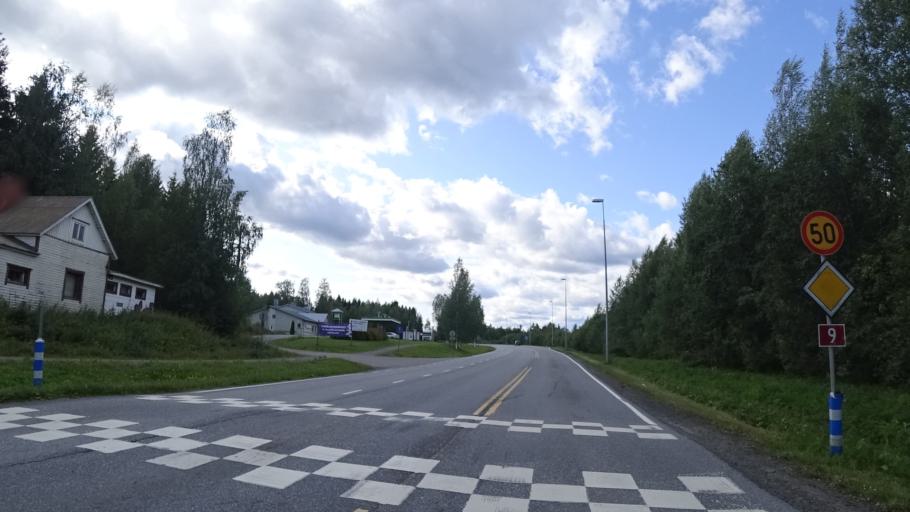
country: RU
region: Republic of Karelia
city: Vyartsilya
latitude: 62.1756
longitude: 30.5921
